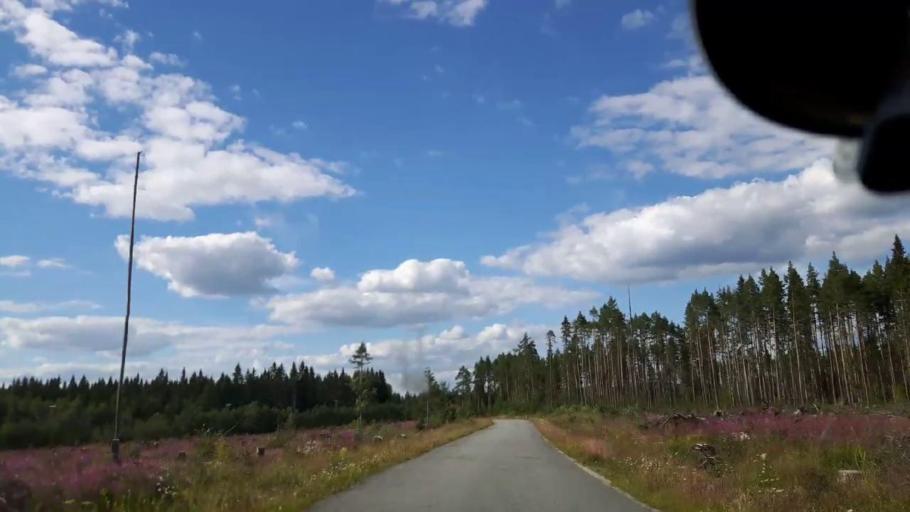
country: SE
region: Jaemtland
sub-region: Braecke Kommun
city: Braecke
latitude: 62.8378
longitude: 15.3036
